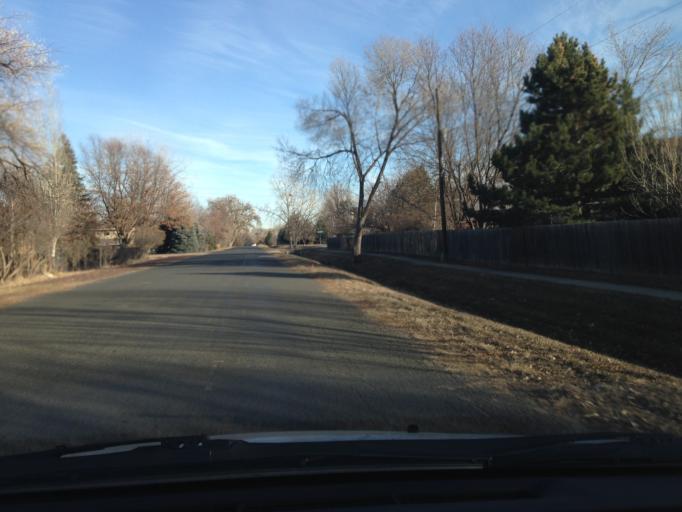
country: US
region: Colorado
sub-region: Boulder County
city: Niwot
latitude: 40.1052
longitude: -105.1659
